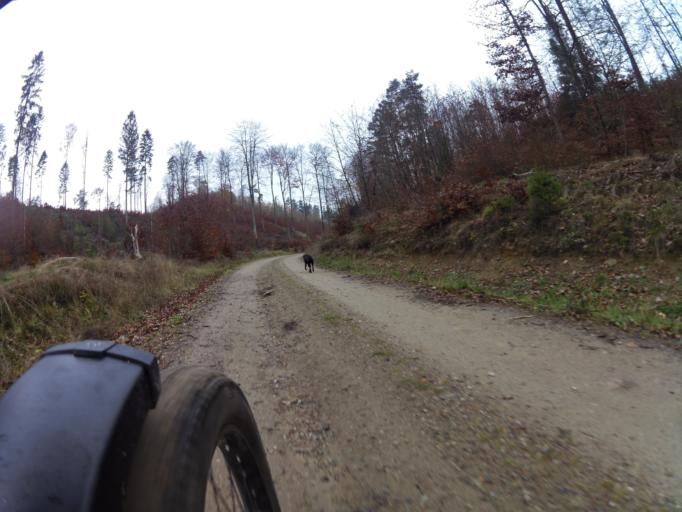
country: PL
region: Pomeranian Voivodeship
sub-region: Powiat pucki
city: Krokowa
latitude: 54.7121
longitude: 18.1431
